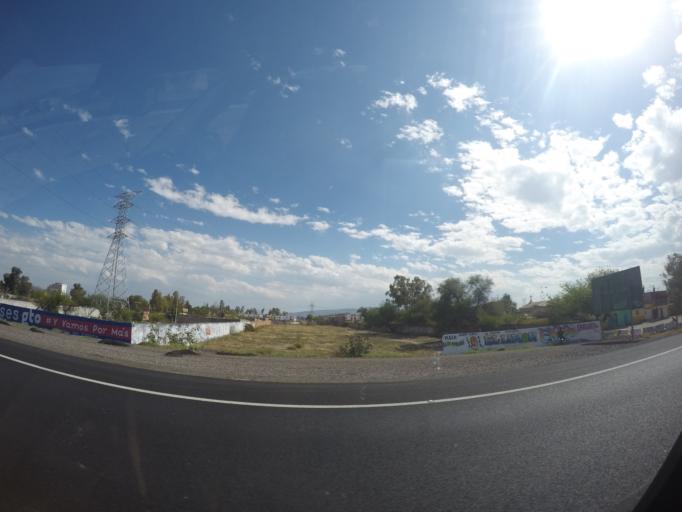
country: MX
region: Guanajuato
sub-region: Celaya
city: Roque
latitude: 20.5605
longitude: -100.8421
